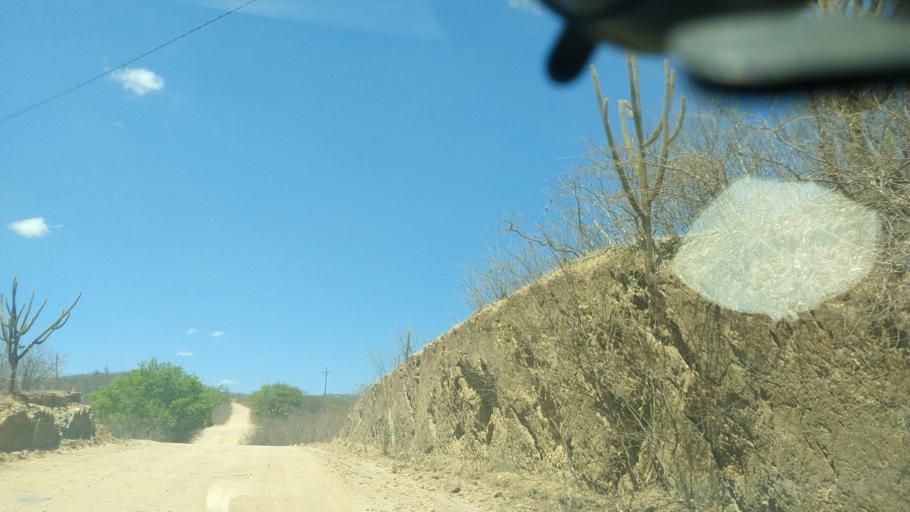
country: BR
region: Rio Grande do Norte
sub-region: Cerro Cora
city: Cerro Cora
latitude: -6.0122
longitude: -36.2975
